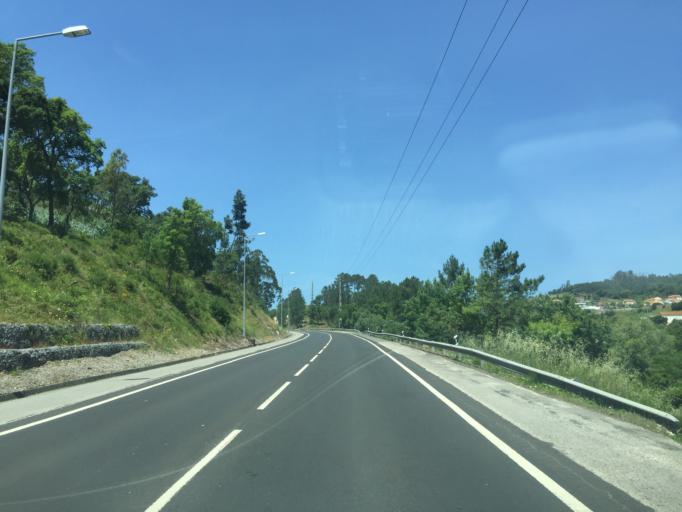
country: PT
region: Lisbon
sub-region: Mafra
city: Venda do Pinheiro
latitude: 38.8963
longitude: -9.2025
